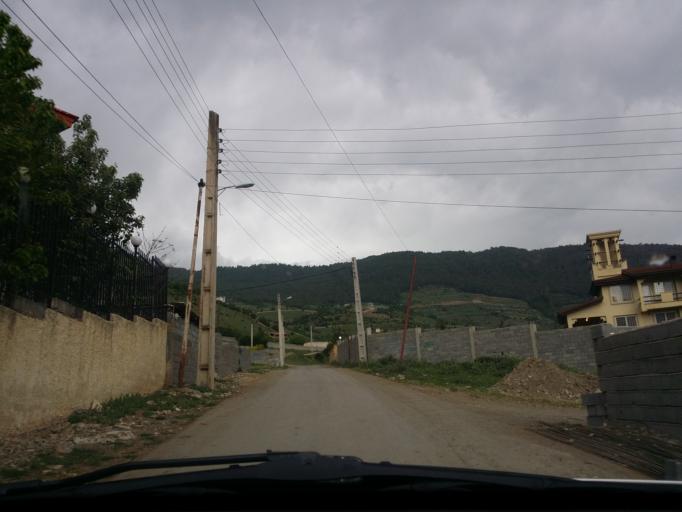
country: IR
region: Mazandaran
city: `Abbasabad
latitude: 36.5064
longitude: 51.1420
